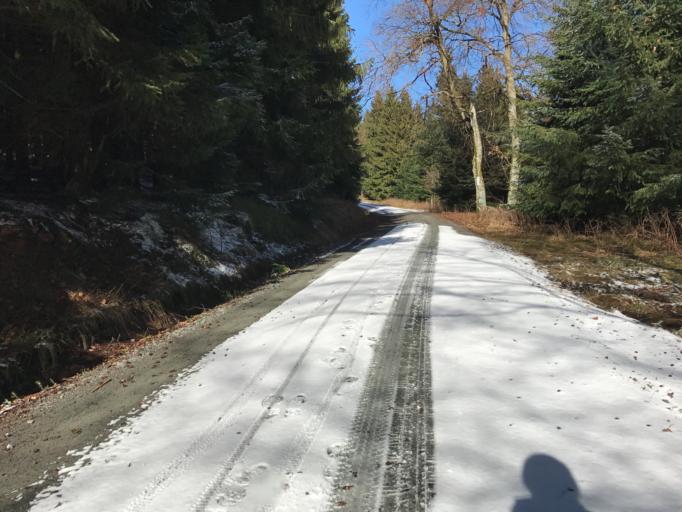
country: DE
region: Hesse
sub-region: Regierungsbezirk Darmstadt
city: Konigstein im Taunus
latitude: 50.2188
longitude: 8.4621
